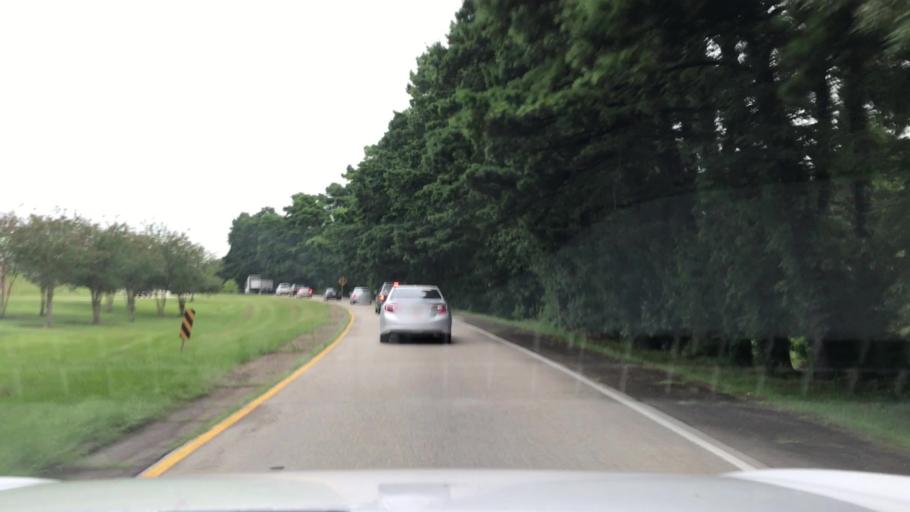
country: US
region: Louisiana
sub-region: East Baton Rouge Parish
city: Brownsfield
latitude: 30.5167
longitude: -91.1580
